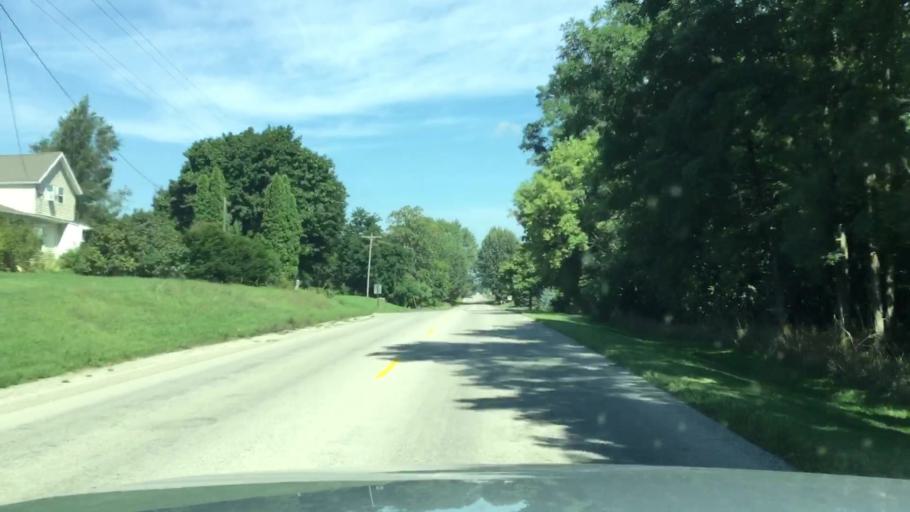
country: US
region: Michigan
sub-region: Lenawee County
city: Manitou Beach-Devils Lake
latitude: 42.0216
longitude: -84.2762
